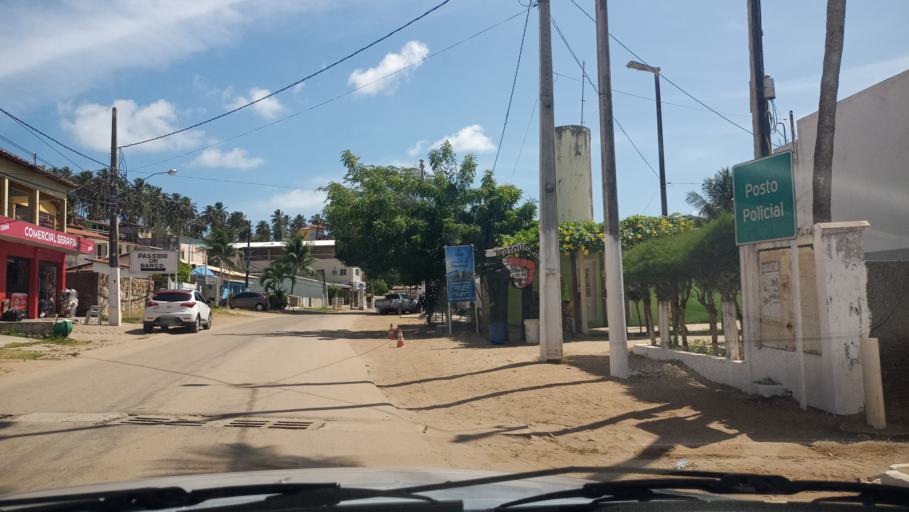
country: BR
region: Rio Grande do Norte
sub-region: Canguaretama
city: Canguaretama
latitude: -6.3137
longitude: -35.0418
